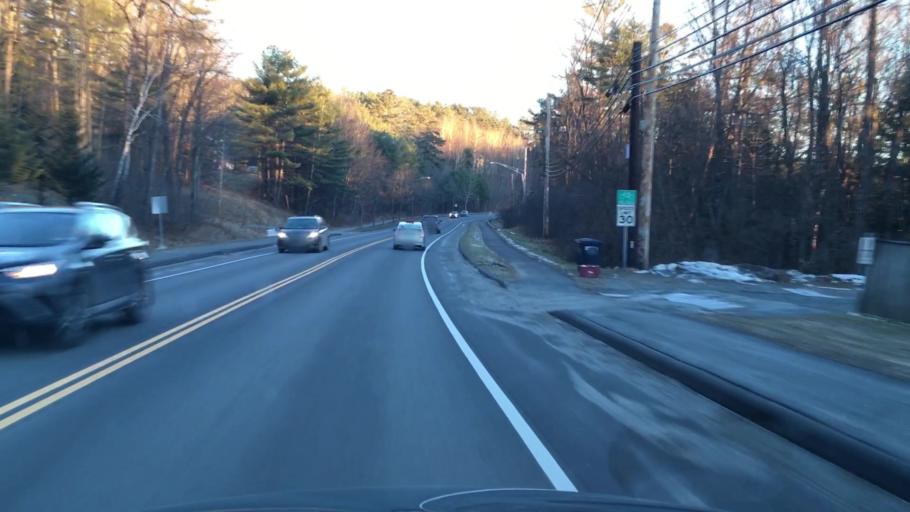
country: US
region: New Hampshire
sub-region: Grafton County
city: Hanover
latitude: 43.6935
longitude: -72.2761
